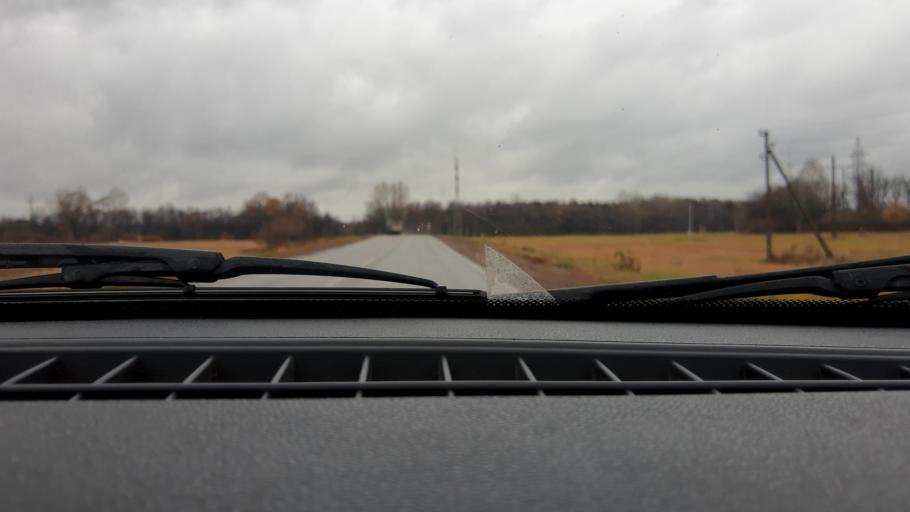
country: RU
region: Bashkortostan
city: Mikhaylovka
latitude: 54.8352
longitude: 55.7925
